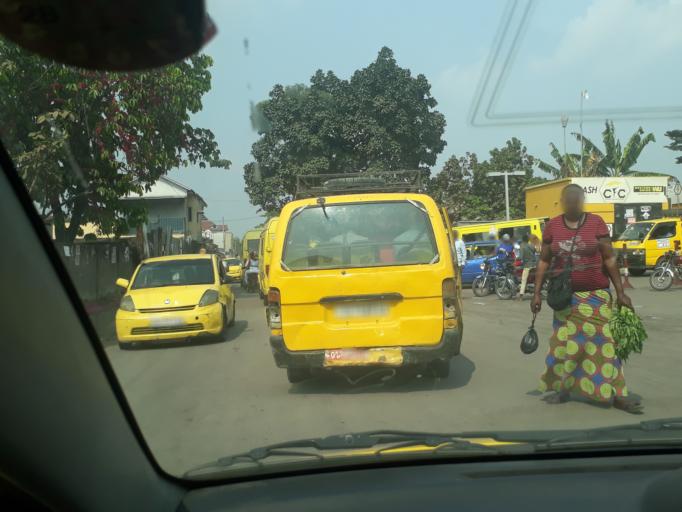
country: CD
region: Kinshasa
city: Kinshasa
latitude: -4.3236
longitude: 15.3183
